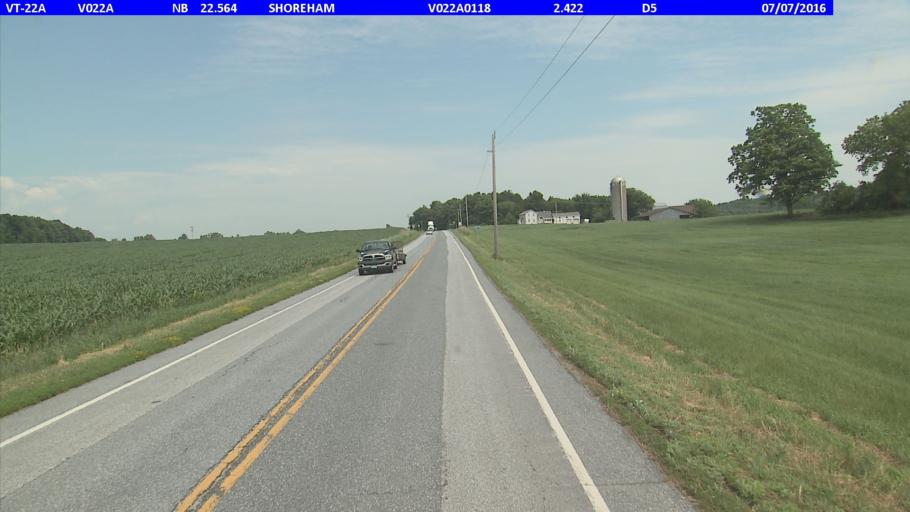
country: US
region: New York
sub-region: Essex County
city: Ticonderoga
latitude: 43.8844
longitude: -73.3094
